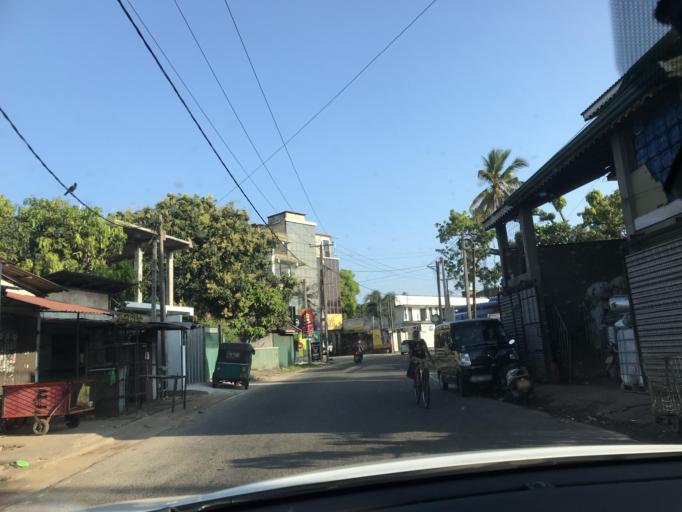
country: LK
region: Western
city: Ja Ela
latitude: 7.0860
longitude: 79.8928
